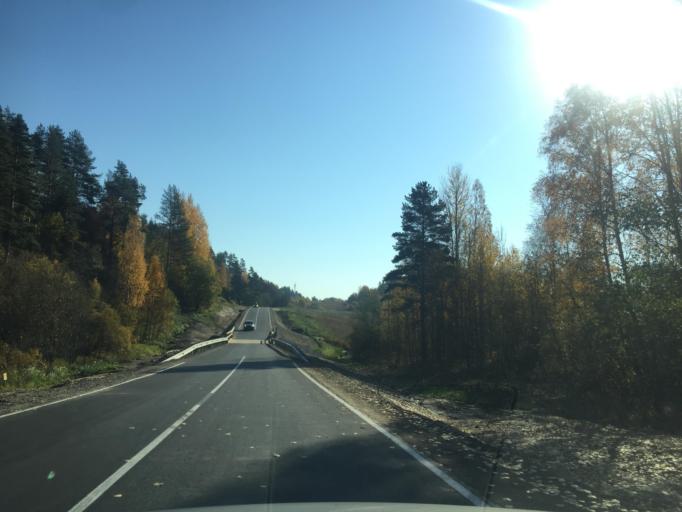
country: RU
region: Leningrad
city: Kuznechnoye
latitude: 61.3170
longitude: 29.8720
